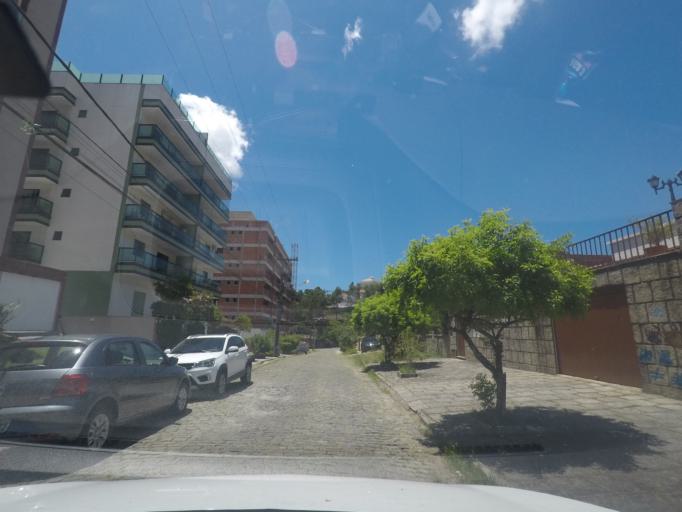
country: BR
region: Rio de Janeiro
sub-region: Teresopolis
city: Teresopolis
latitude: -22.4301
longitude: -42.9823
